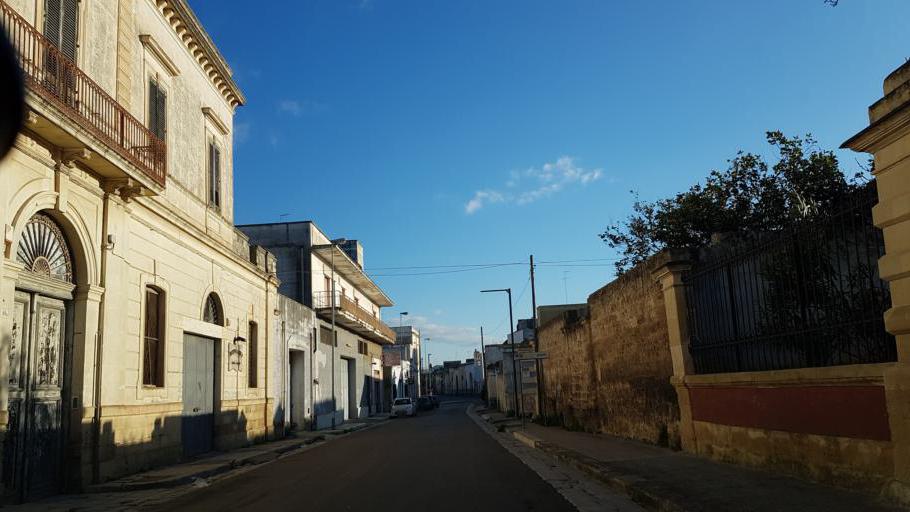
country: IT
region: Apulia
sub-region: Provincia di Lecce
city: Squinzano
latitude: 40.4387
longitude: 18.0462
